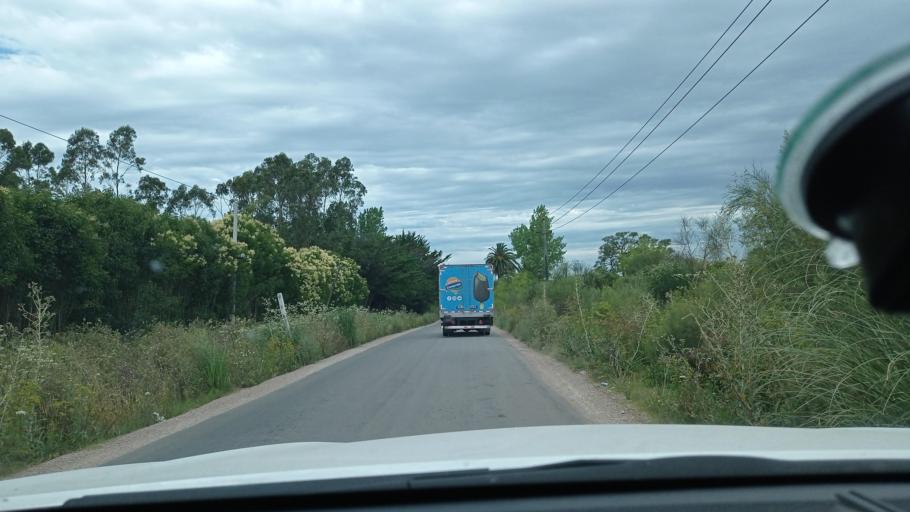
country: UY
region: Canelones
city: La Paz
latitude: -34.7979
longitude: -56.1943
